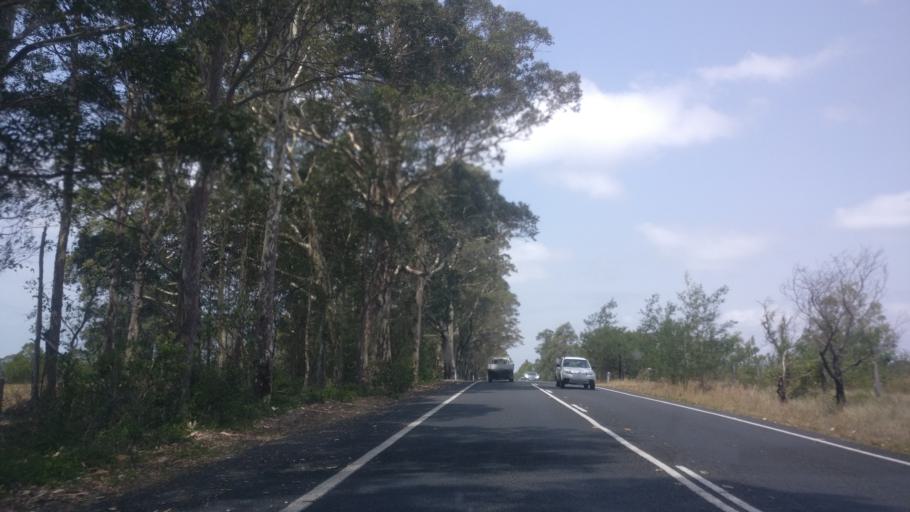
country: AU
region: New South Wales
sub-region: Shoalhaven Shire
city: Bomaderry
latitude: -34.8278
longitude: 150.5753
